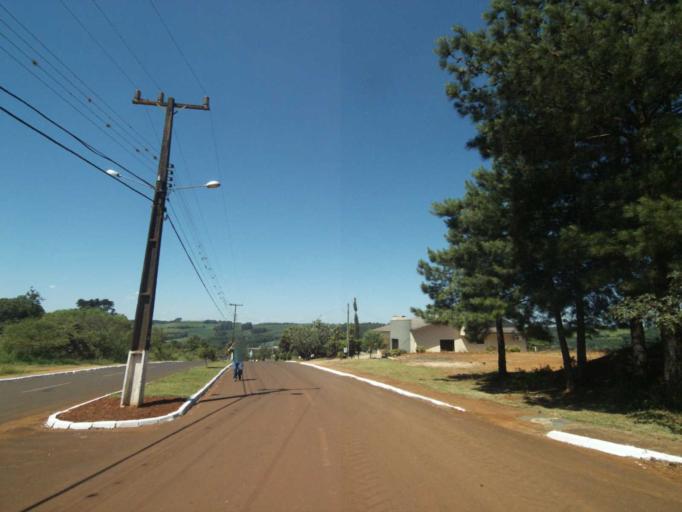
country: BR
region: Parana
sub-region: Laranjeiras Do Sul
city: Laranjeiras do Sul
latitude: -25.3850
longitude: -52.2076
